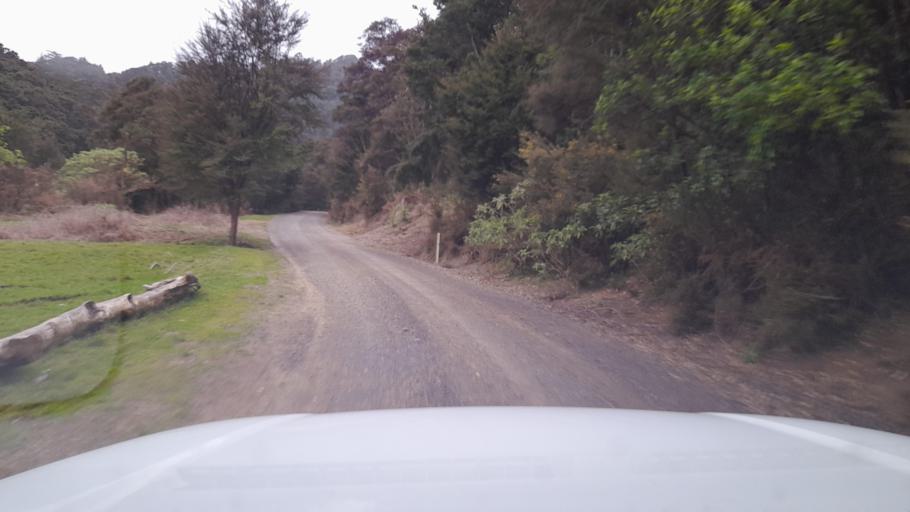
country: NZ
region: Northland
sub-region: Far North District
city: Paihia
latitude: -35.3545
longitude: 174.2327
